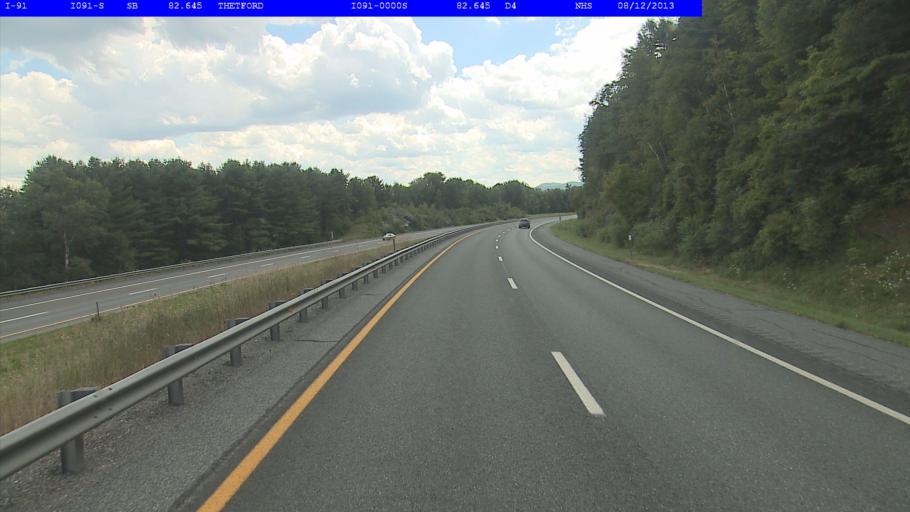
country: US
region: New Hampshire
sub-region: Grafton County
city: Lyme
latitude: 43.7913
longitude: -72.2143
